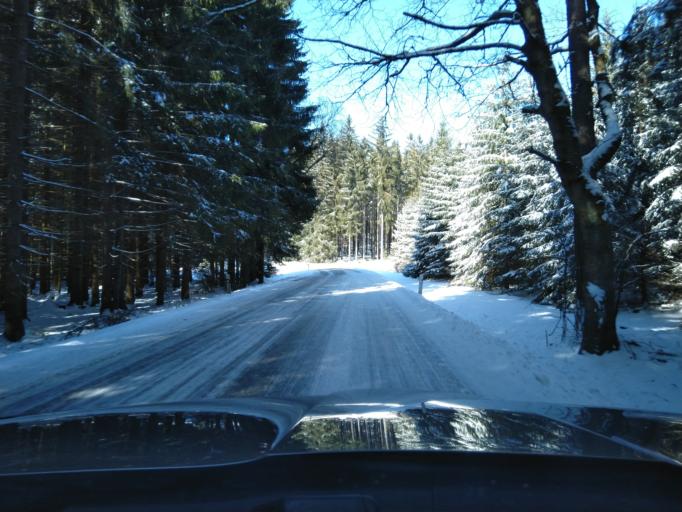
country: CZ
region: Jihocesky
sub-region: Okres Prachatice
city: Stachy
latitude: 49.0577
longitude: 13.6467
